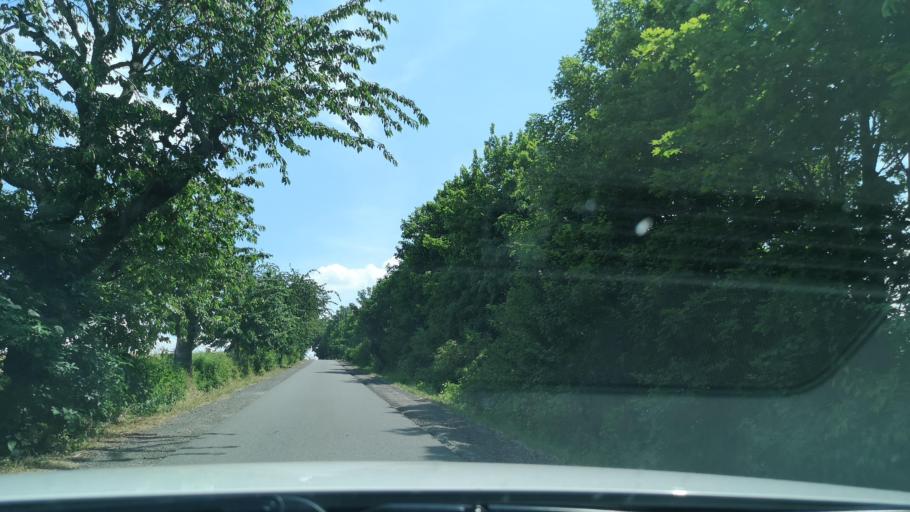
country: DE
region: Thuringia
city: Eberstedt
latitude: 51.0515
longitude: 11.5829
